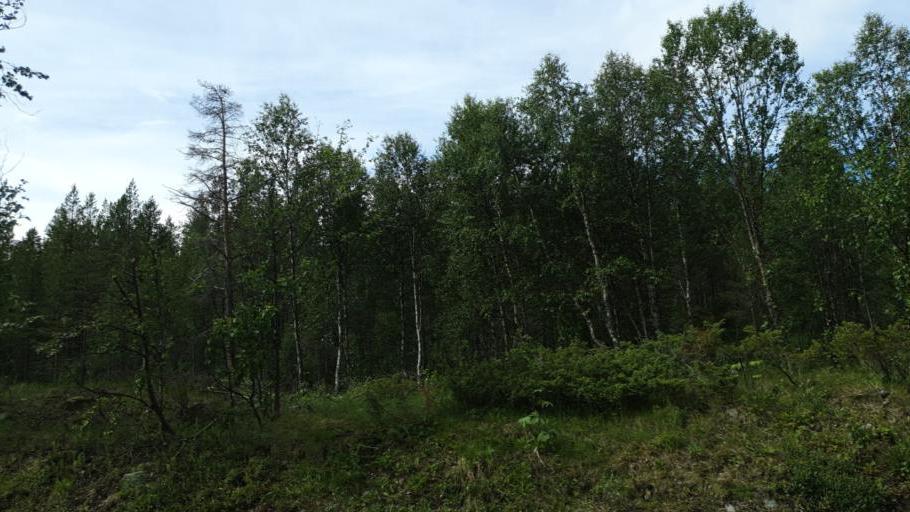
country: NO
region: Oppland
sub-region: Vaga
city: Vagamo
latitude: 61.7006
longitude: 9.0591
